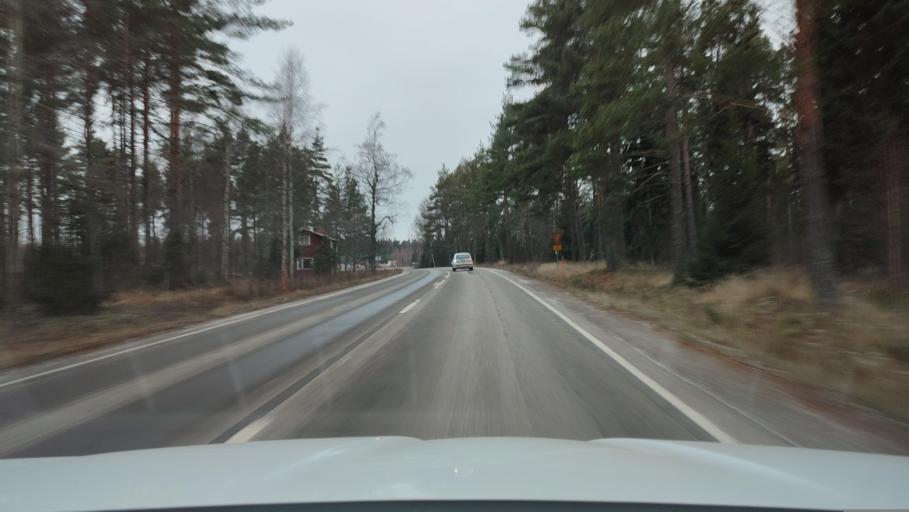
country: FI
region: Ostrobothnia
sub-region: Sydosterbotten
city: Naerpes
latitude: 62.3972
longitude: 21.3676
